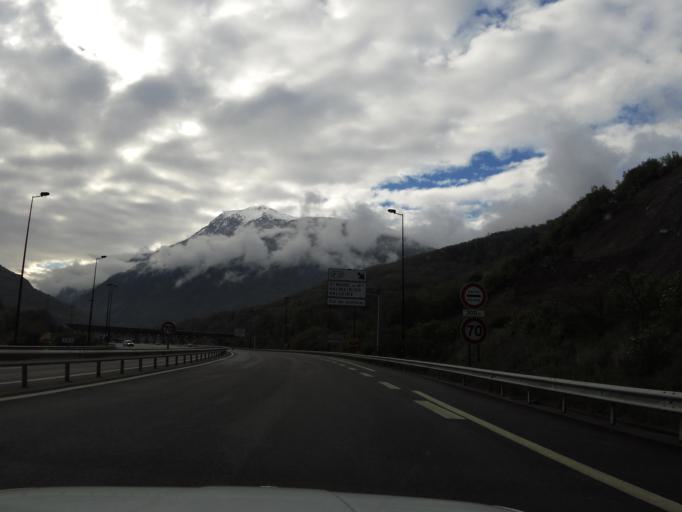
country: FR
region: Rhone-Alpes
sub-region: Departement de la Savoie
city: Saint-Michel-de-Maurienne
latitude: 45.2203
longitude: 6.4553
